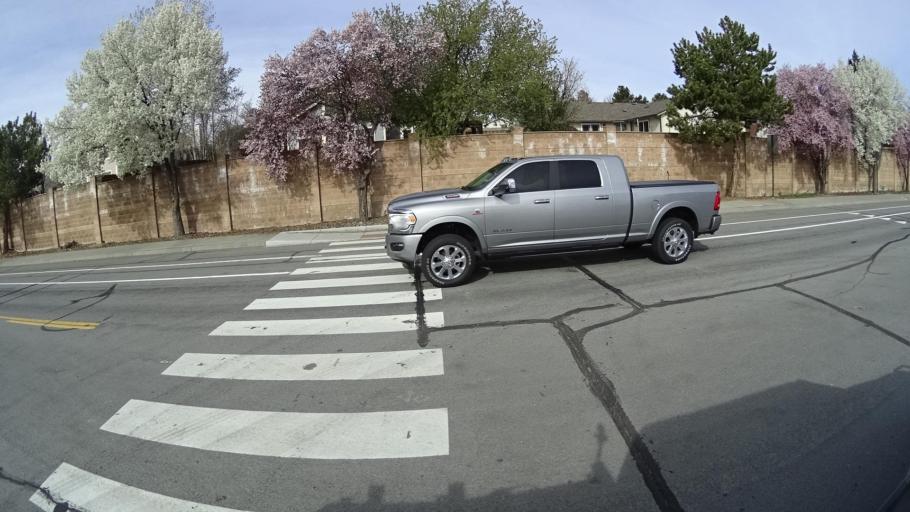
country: US
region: Nevada
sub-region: Washoe County
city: Mogul
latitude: 39.5235
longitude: -119.8952
